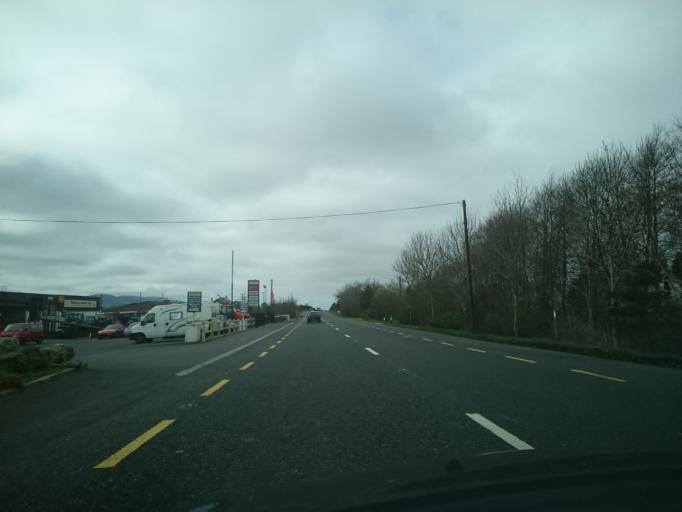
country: IE
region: Connaught
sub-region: Maigh Eo
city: Westport
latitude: 53.8034
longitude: -9.4733
